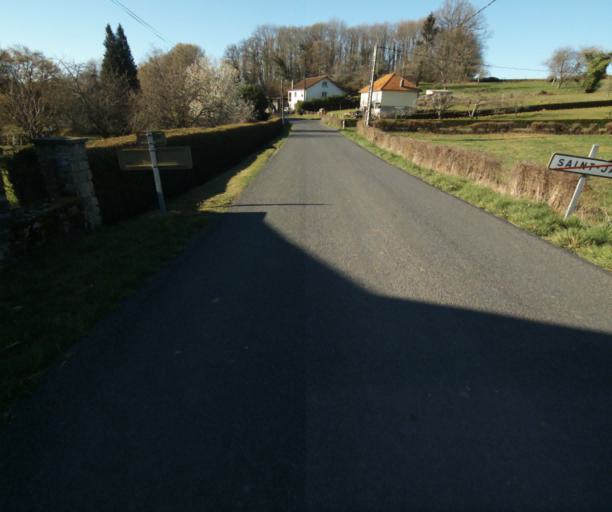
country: FR
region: Limousin
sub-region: Departement de la Correze
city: Saint-Clement
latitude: 45.3941
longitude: 1.6419
